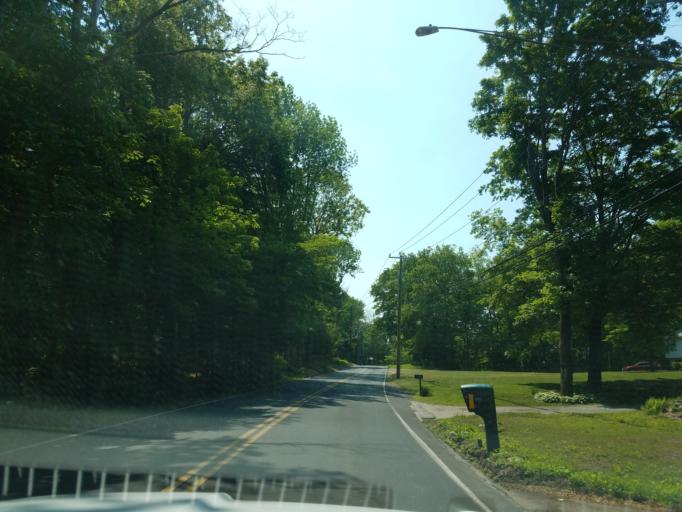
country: US
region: Connecticut
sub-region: New London County
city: Montville Center
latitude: 41.4948
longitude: -72.2113
